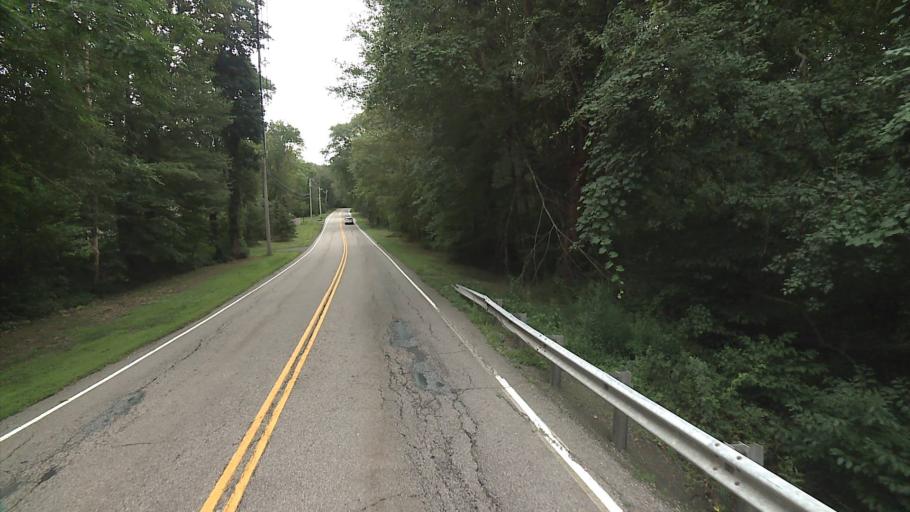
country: US
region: Connecticut
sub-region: Middlesex County
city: Essex Village
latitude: 41.3545
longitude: -72.3403
